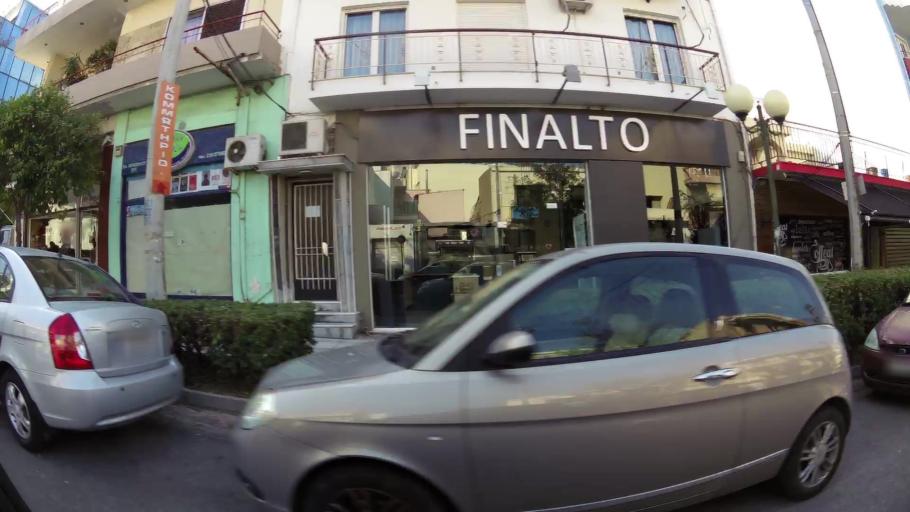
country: GR
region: Attica
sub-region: Nomarchia Athinas
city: Nea Ionia
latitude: 38.0467
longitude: 23.7508
